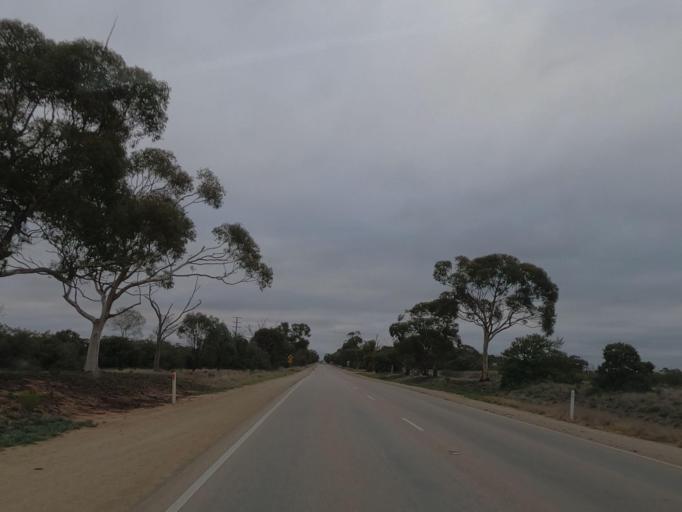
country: AU
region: Victoria
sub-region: Swan Hill
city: Swan Hill
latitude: -35.4058
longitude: 143.5813
